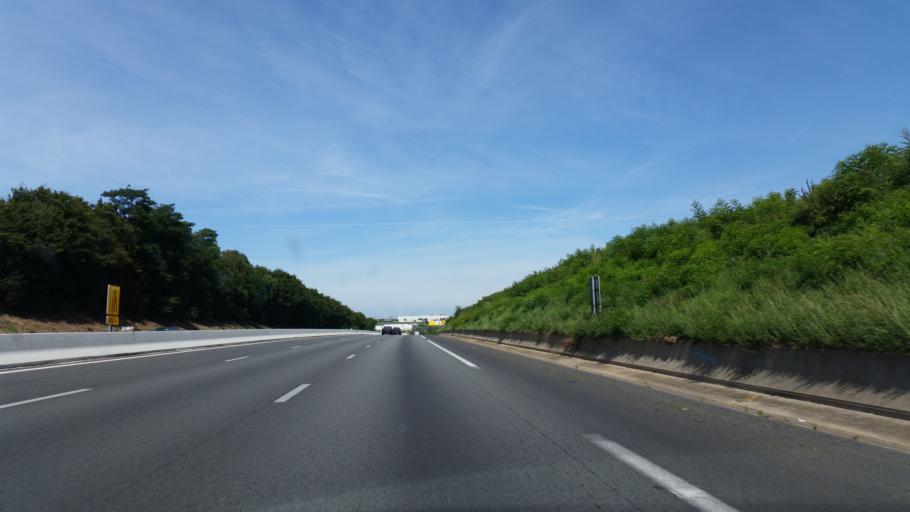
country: FR
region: Nord-Pas-de-Calais
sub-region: Departement du Pas-de-Calais
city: Croisilles
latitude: 50.2426
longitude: 2.8552
